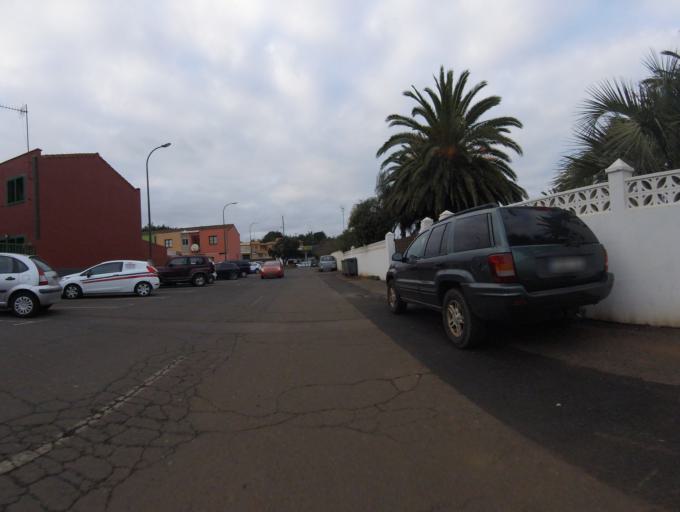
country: ES
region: Canary Islands
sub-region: Provincia de Santa Cruz de Tenerife
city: La Laguna
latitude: 28.4553
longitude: -16.3615
